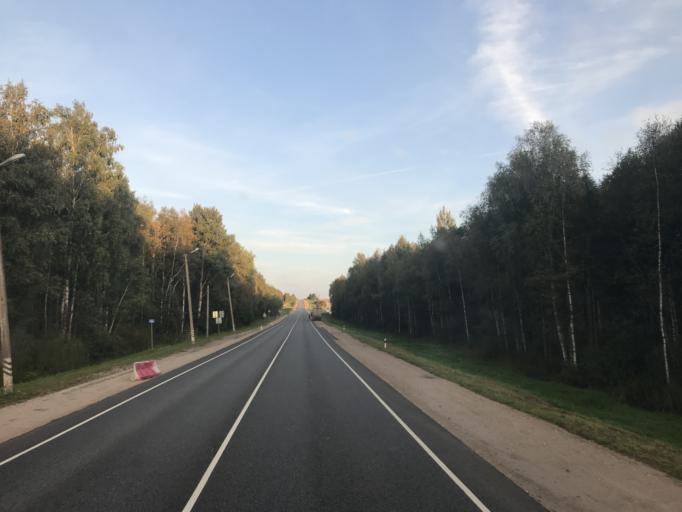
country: RU
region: Smolensk
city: Rudnya
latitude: 54.9856
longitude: 30.9627
